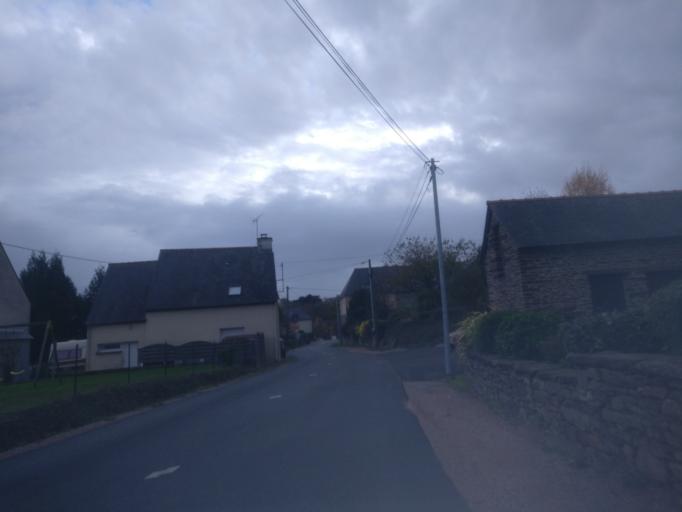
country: FR
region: Brittany
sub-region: Departement d'Ille-et-Vilaine
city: Guichen
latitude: 48.0078
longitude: -1.7911
